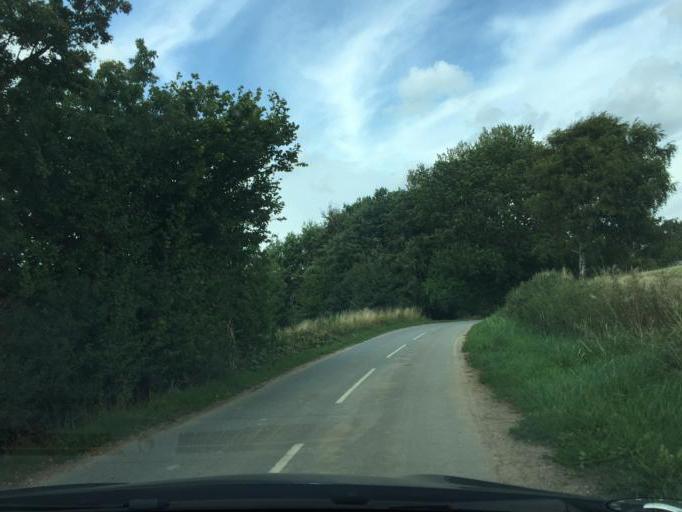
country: DK
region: South Denmark
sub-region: Assens Kommune
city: Tommerup Stationsby
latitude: 55.3756
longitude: 10.1710
